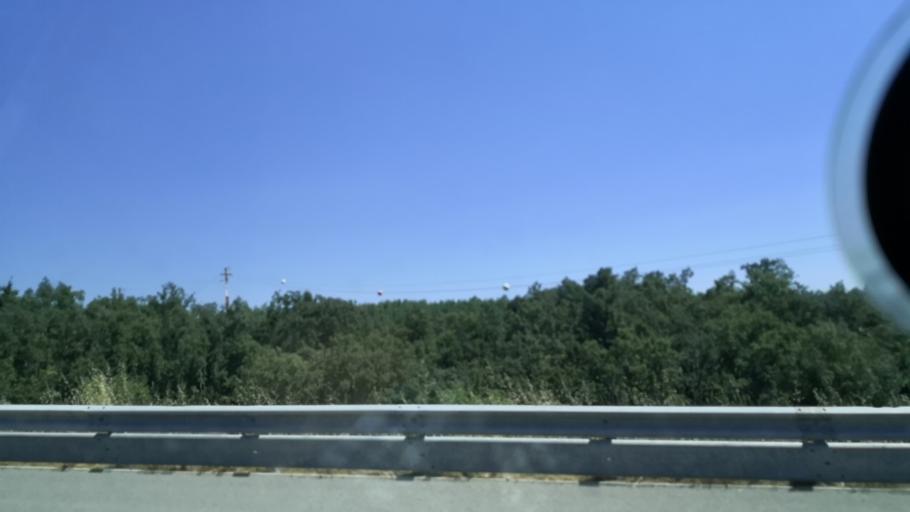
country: PT
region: Braganca
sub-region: Braganca Municipality
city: Braganca
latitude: 41.7213
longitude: -6.8113
